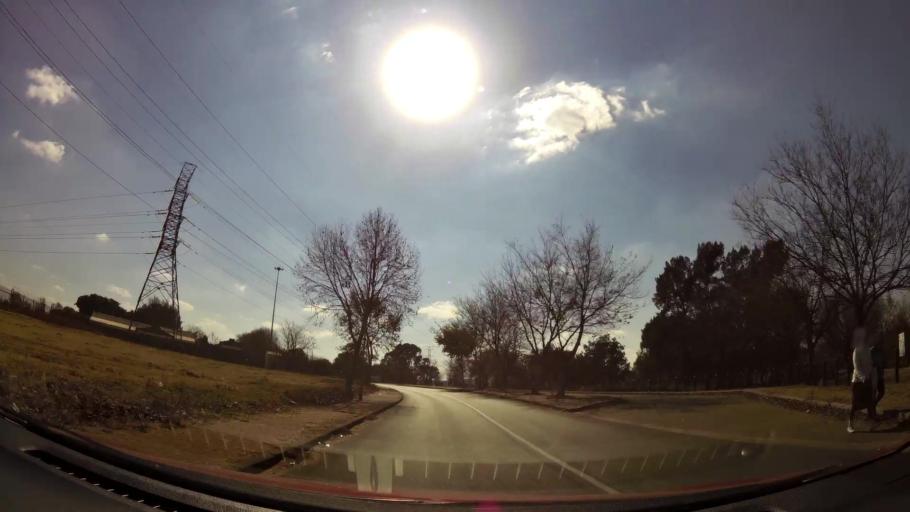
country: ZA
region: Gauteng
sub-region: City of Johannesburg Metropolitan Municipality
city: Soweto
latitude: -26.2441
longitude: 27.8880
